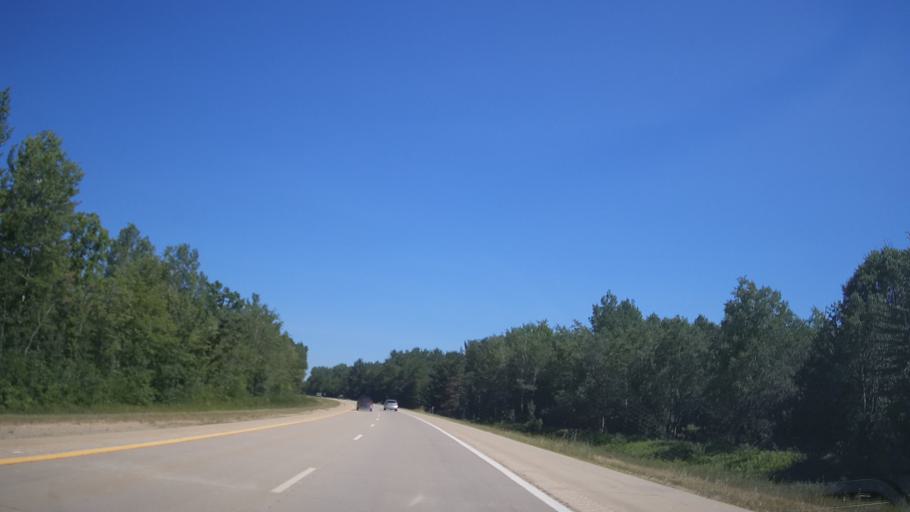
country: US
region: Michigan
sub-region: Midland County
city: Coleman
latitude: 43.7489
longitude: -84.5396
